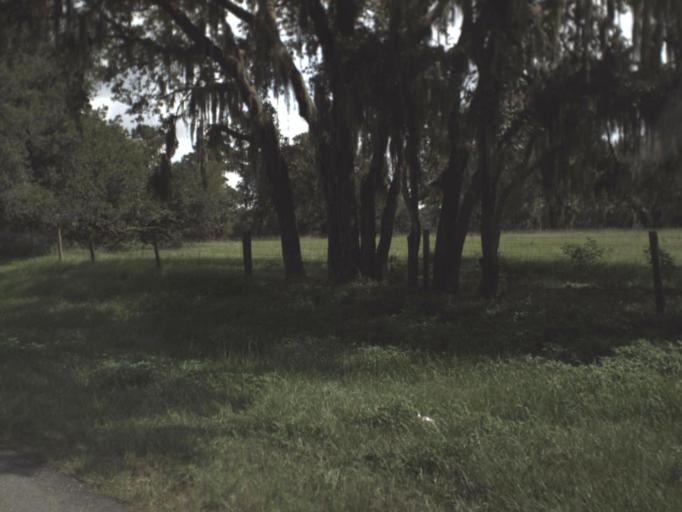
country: US
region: Florida
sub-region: Pasco County
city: Zephyrhills South
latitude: 28.2089
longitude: -82.1757
